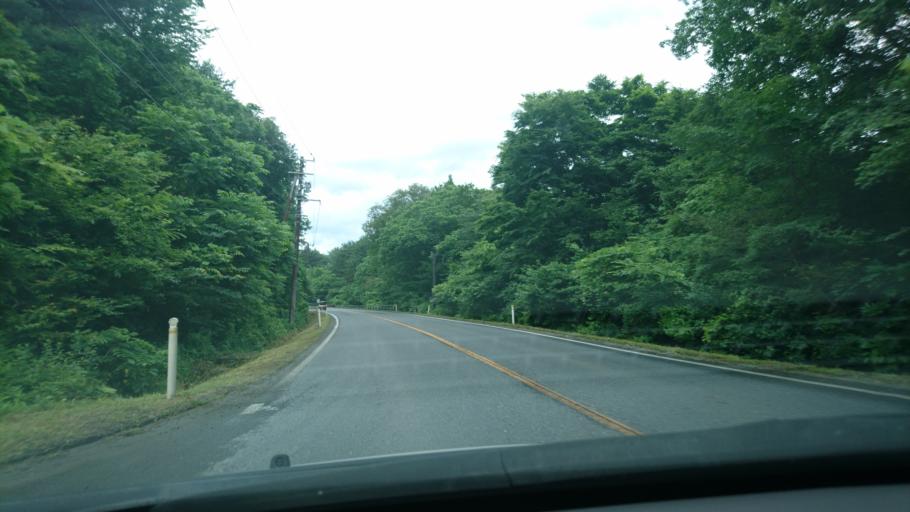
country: JP
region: Iwate
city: Otsuchi
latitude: 39.4020
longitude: 141.9543
